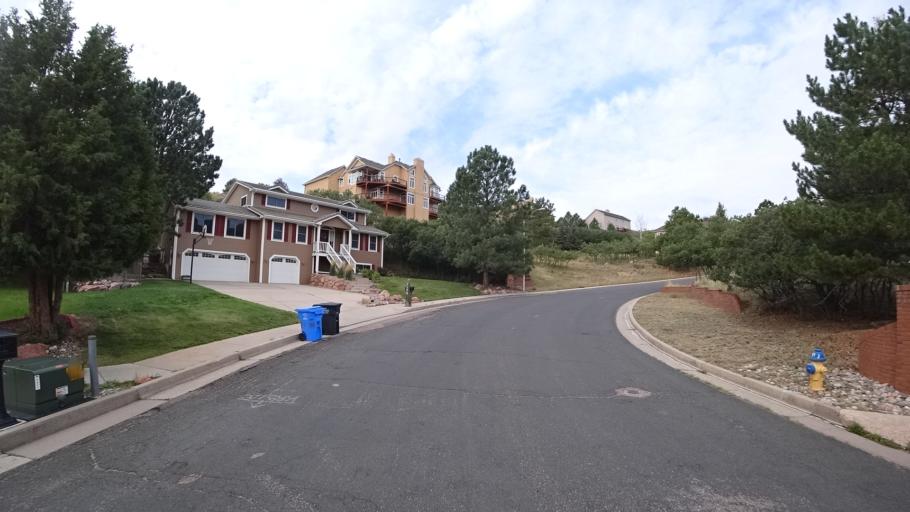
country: US
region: Colorado
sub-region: El Paso County
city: Air Force Academy
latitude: 38.9358
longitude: -104.8631
